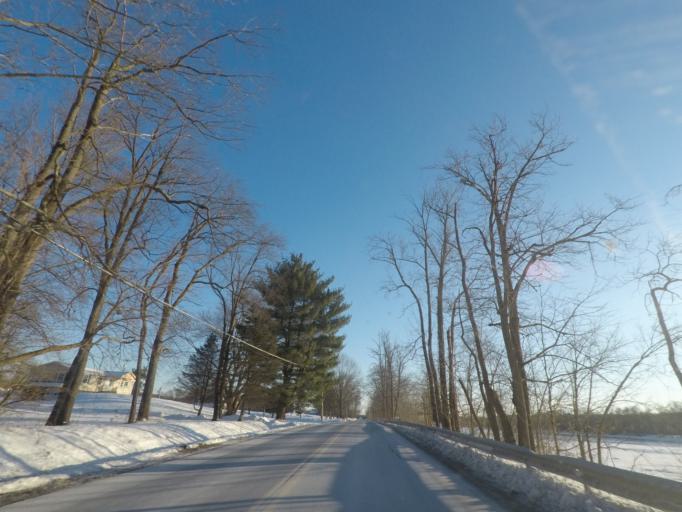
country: US
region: New York
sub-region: Saratoga County
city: Mechanicville
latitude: 42.8564
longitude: -73.6719
